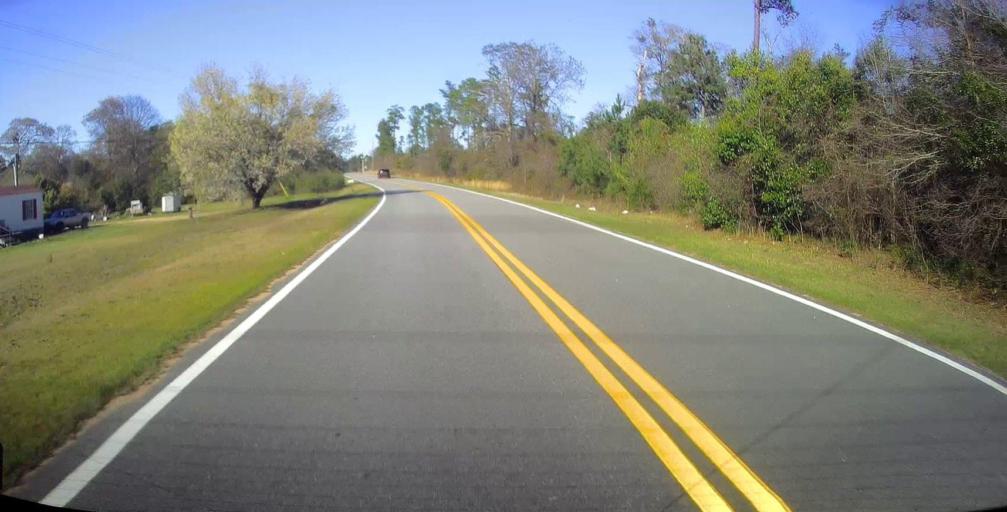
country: US
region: Georgia
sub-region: Peach County
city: Byron
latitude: 32.6788
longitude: -83.8089
